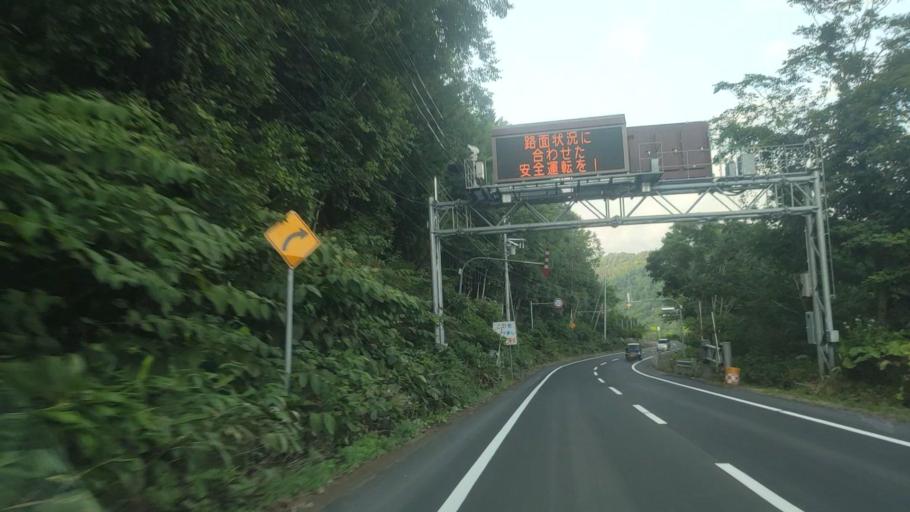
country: JP
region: Hokkaido
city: Bibai
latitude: 43.2458
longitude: 142.0197
